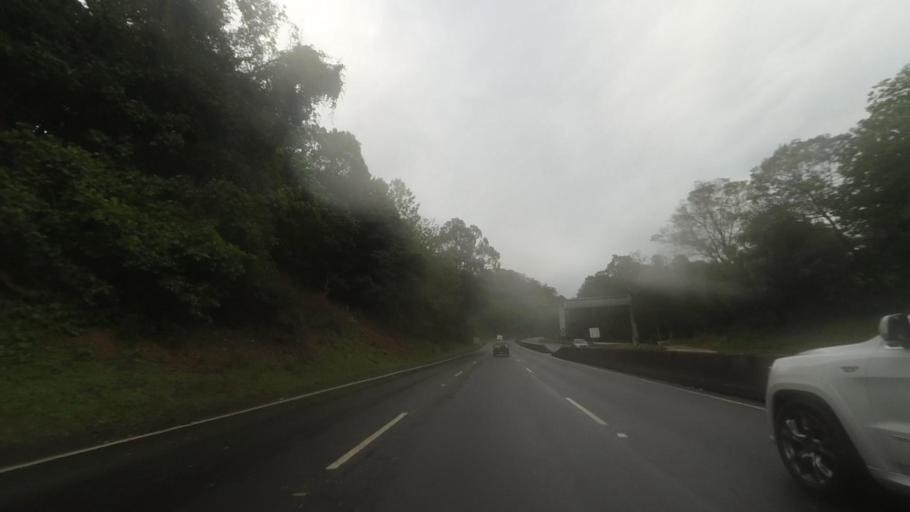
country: AU
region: New South Wales
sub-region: Wollongong
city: Mount Ousley
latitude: -34.3905
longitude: 150.8580
